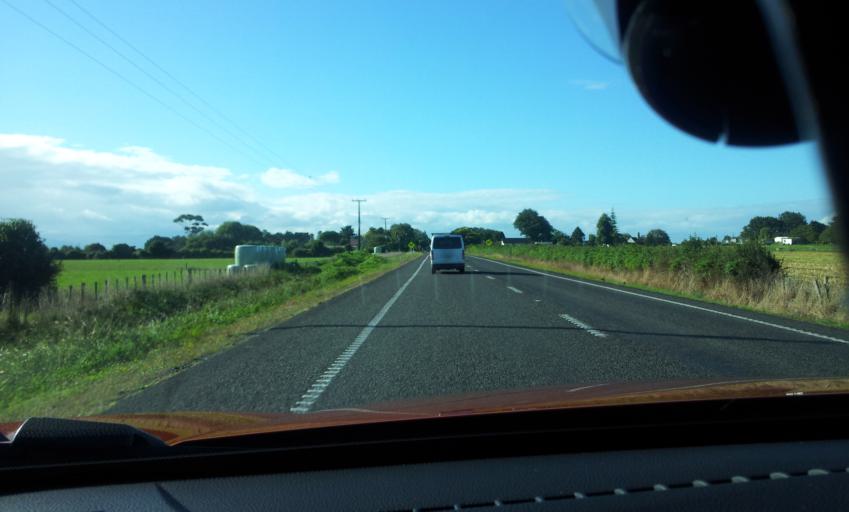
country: NZ
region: Waikato
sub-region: Hauraki District
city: Ngatea
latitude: -37.3973
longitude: 175.4648
